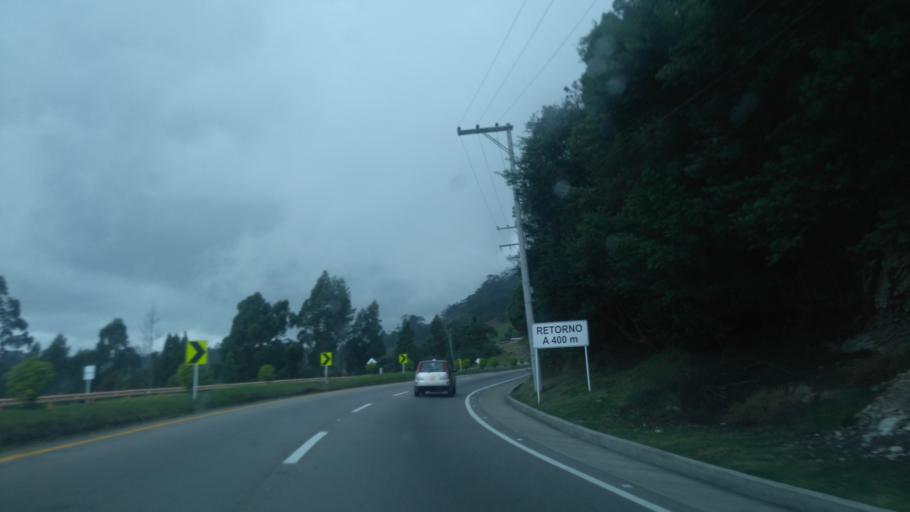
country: CO
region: Cundinamarca
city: El Rosal
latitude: 4.8848
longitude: -74.3002
